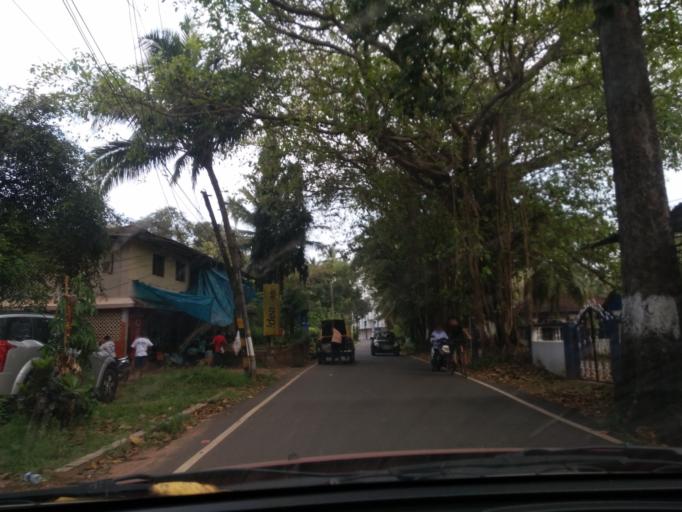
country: IN
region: Goa
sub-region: South Goa
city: Benaulim
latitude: 15.2684
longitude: 73.9287
